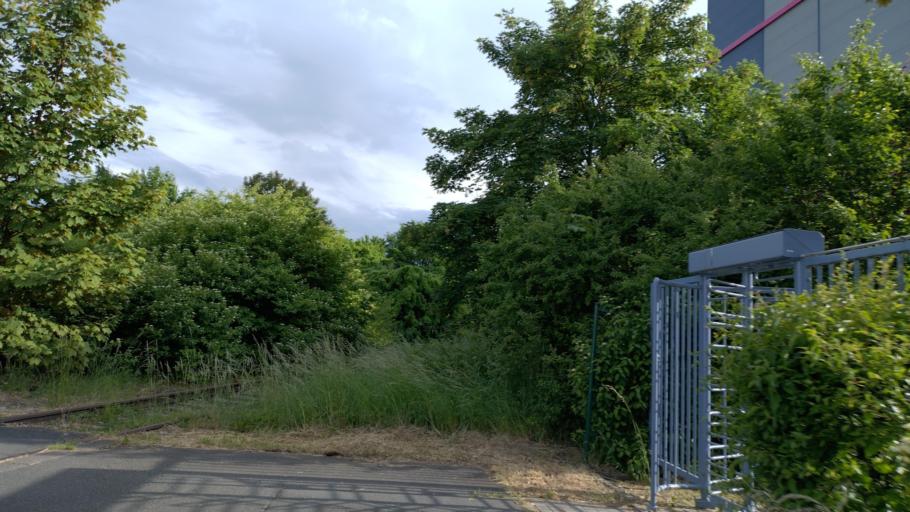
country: DE
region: Bavaria
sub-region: Upper Franconia
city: Bindlach
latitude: 49.9592
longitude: 11.6142
